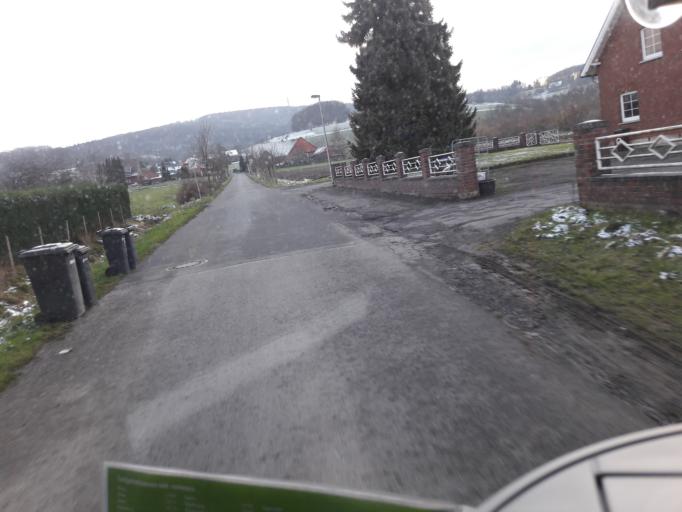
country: DE
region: Lower Saxony
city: Buckeburg
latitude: 52.2347
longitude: 9.0592
